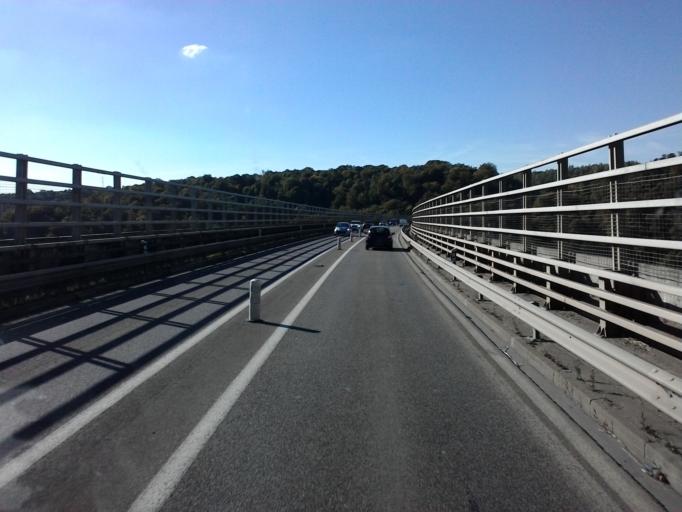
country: FR
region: Lorraine
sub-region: Departement de Meurthe-et-Moselle
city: Rehon
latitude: 49.5052
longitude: 5.7591
